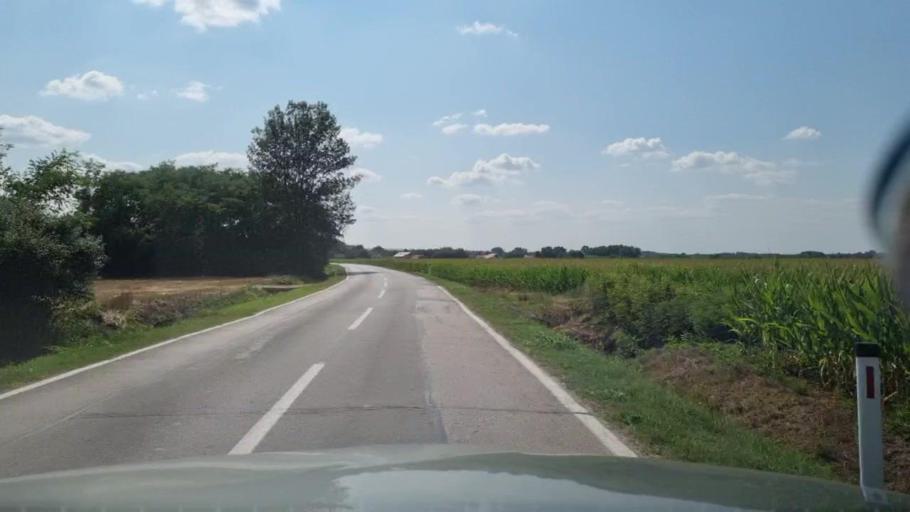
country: BA
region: Federation of Bosnia and Herzegovina
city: Donja Dubica
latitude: 45.0605
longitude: 18.3980
